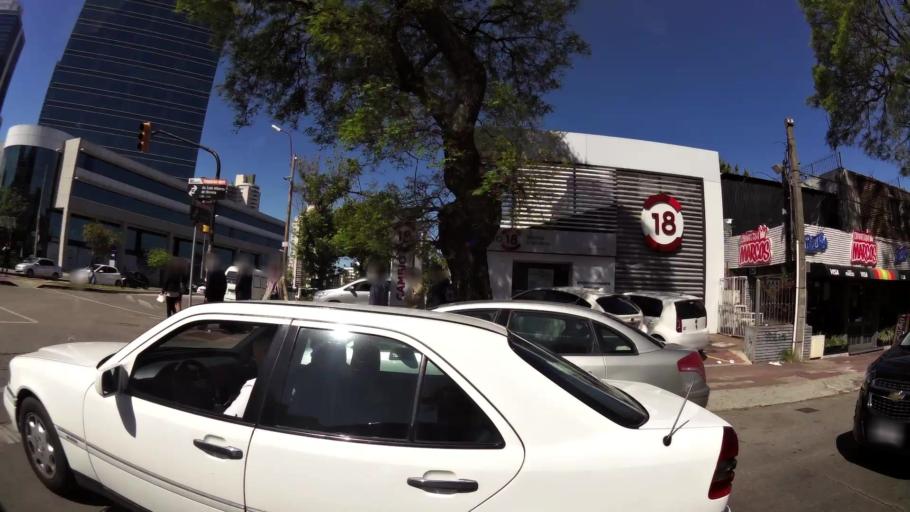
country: UY
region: Montevideo
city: Montevideo
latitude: -34.9059
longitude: -56.1367
